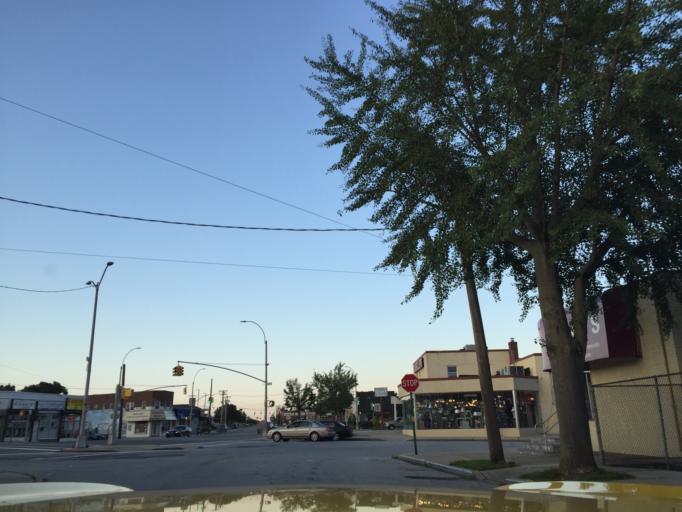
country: US
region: New York
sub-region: Nassau County
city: North New Hyde Park
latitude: 40.7385
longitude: -73.7014
